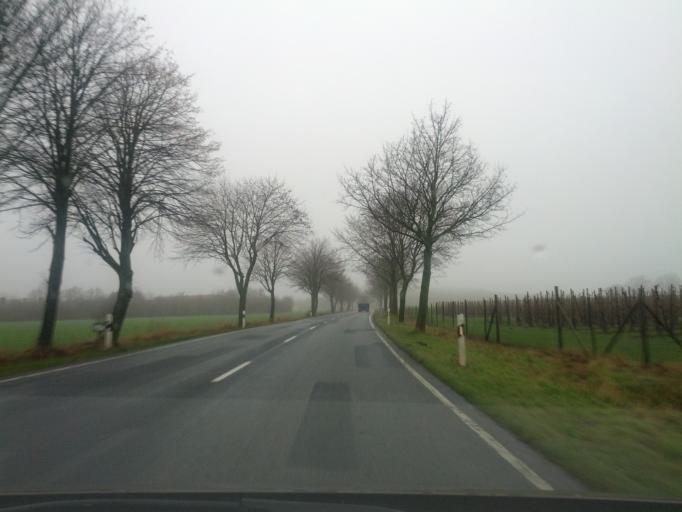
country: DE
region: Lower Saxony
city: Nottensdorf
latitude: 53.4624
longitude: 9.5980
